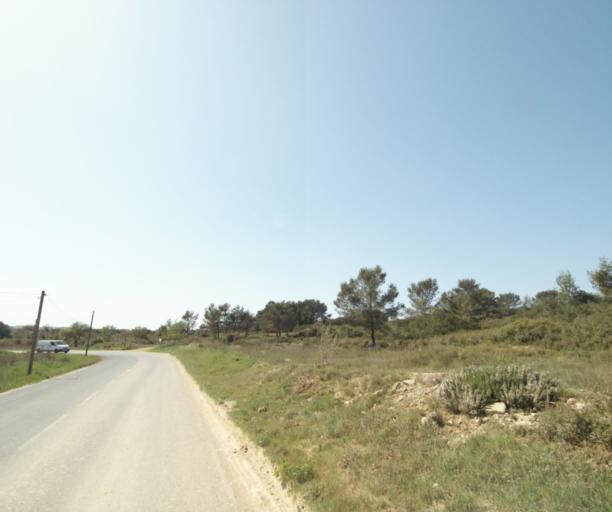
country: FR
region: Languedoc-Roussillon
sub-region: Departement de l'Herault
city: Combaillaux
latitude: 43.6466
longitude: 3.7690
